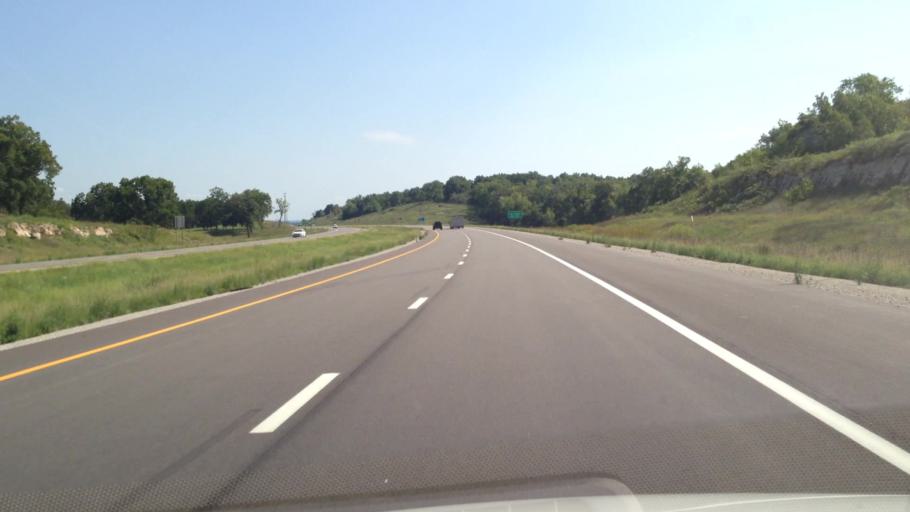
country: US
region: Kansas
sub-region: Linn County
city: La Cygne
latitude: 38.3577
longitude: -94.6876
